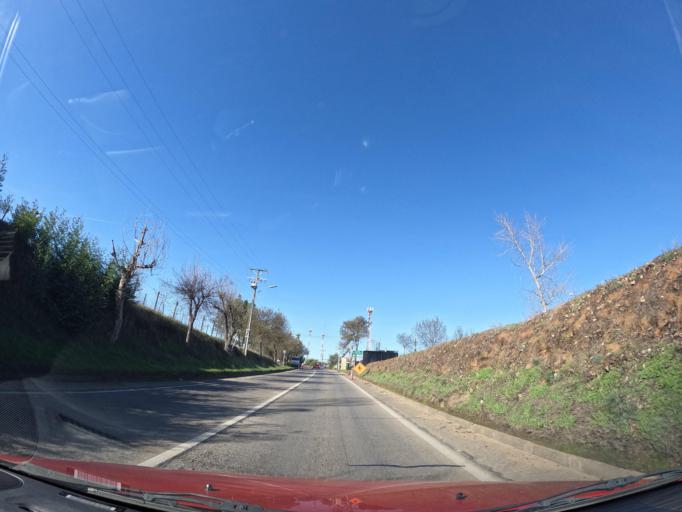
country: CL
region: Maule
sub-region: Provincia de Cauquenes
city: Cauquenes
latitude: -35.9568
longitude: -72.3057
